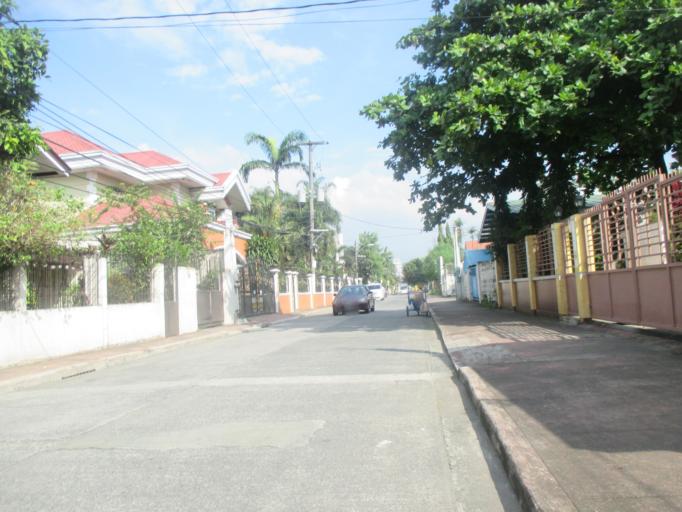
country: PH
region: Metro Manila
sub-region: Marikina
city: Calumpang
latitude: 14.6283
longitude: 121.1003
